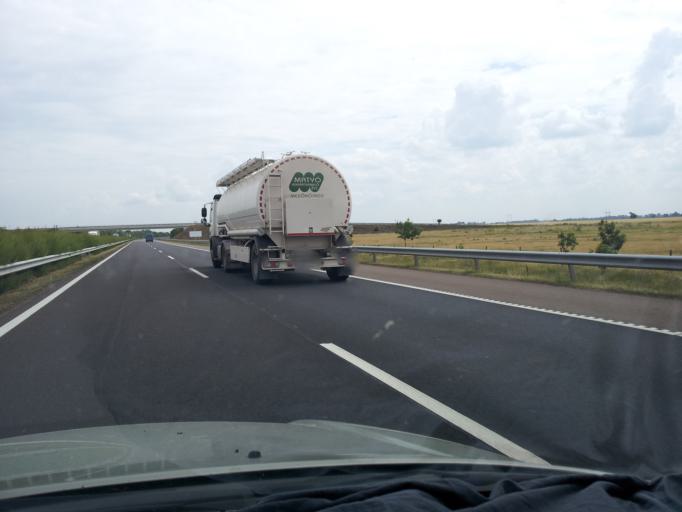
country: HU
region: Borsod-Abauj-Zemplen
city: Szentistvan
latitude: 47.7968
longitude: 20.6427
